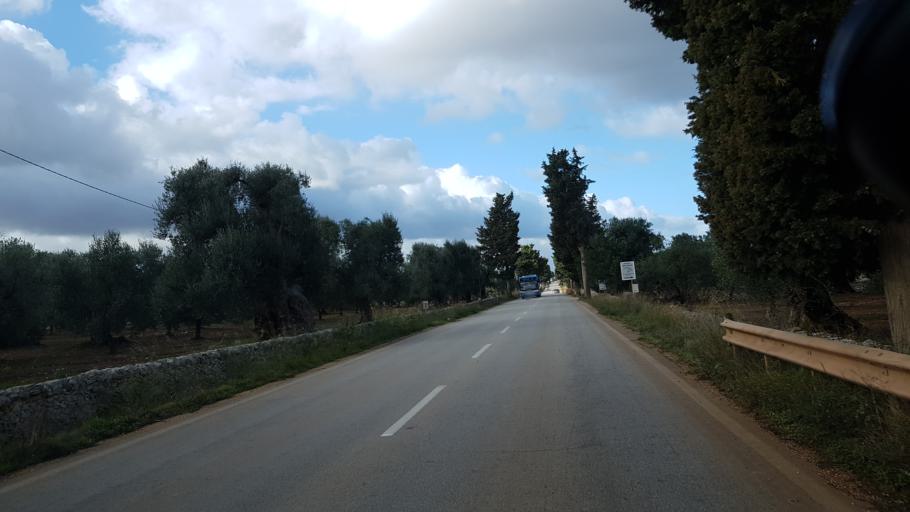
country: IT
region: Apulia
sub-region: Provincia di Brindisi
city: Montalbano
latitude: 40.7758
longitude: 17.4949
